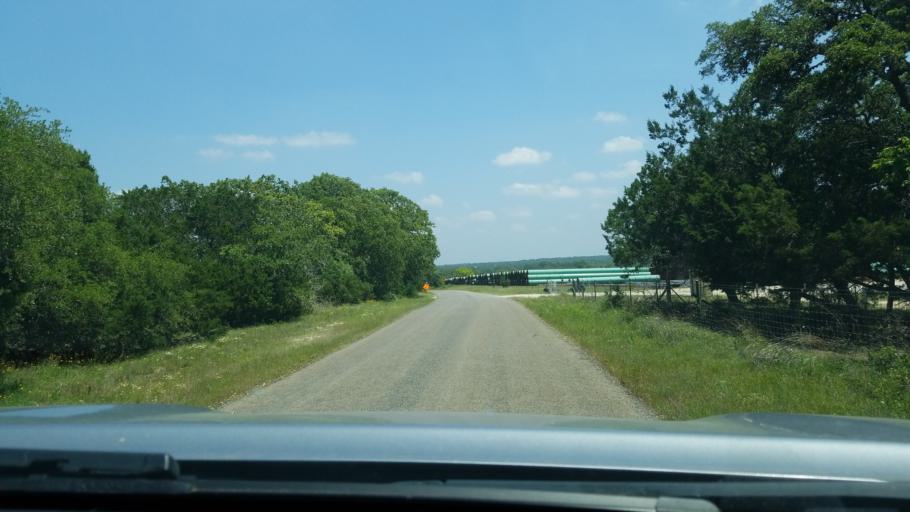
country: US
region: Texas
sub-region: Blanco County
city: Blanco
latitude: 30.0772
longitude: -98.3993
